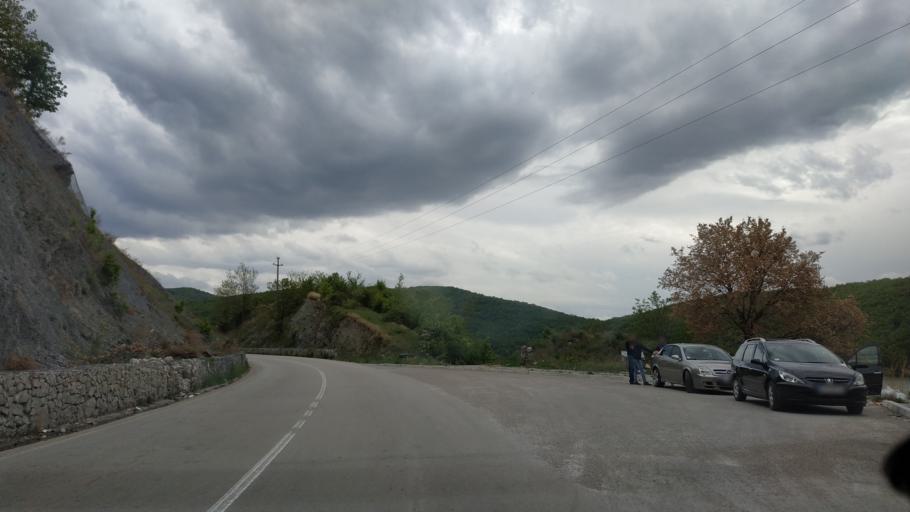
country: RS
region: Central Serbia
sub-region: Nisavski Okrug
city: Aleksinac
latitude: 43.6474
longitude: 21.7124
